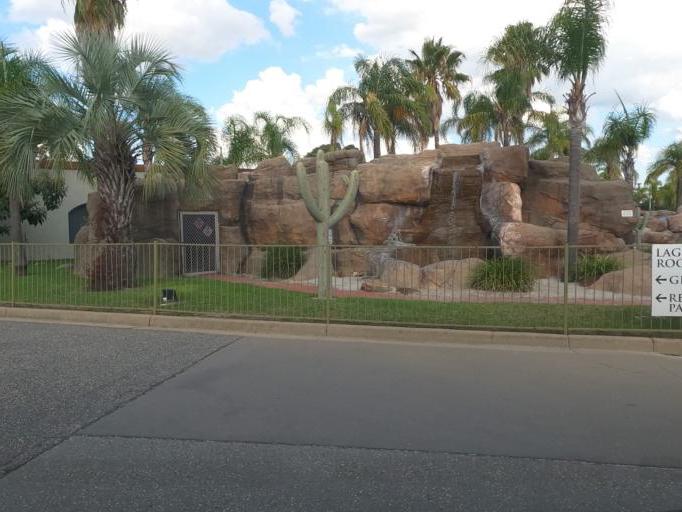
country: AU
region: New South Wales
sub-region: Albury Municipality
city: Lavington
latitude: -36.0461
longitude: 146.9440
